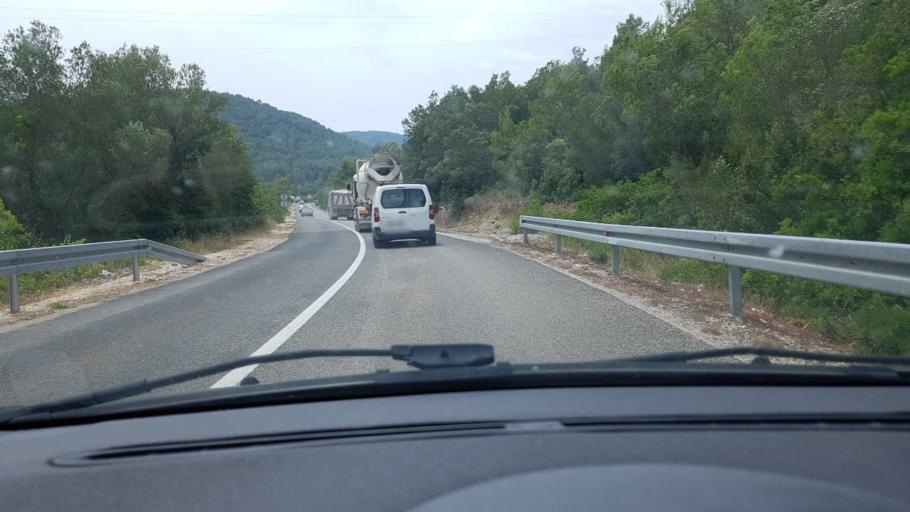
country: HR
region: Dubrovacko-Neretvanska
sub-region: Grad Dubrovnik
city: Vela Luka
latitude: 42.9507
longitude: 16.7824
